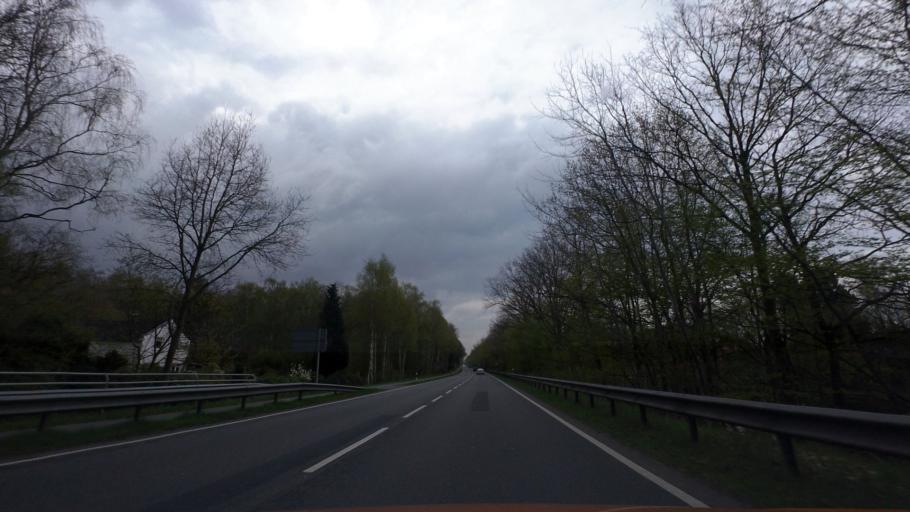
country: DE
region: Lower Saxony
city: Wardenburg
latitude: 53.1081
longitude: 8.1331
